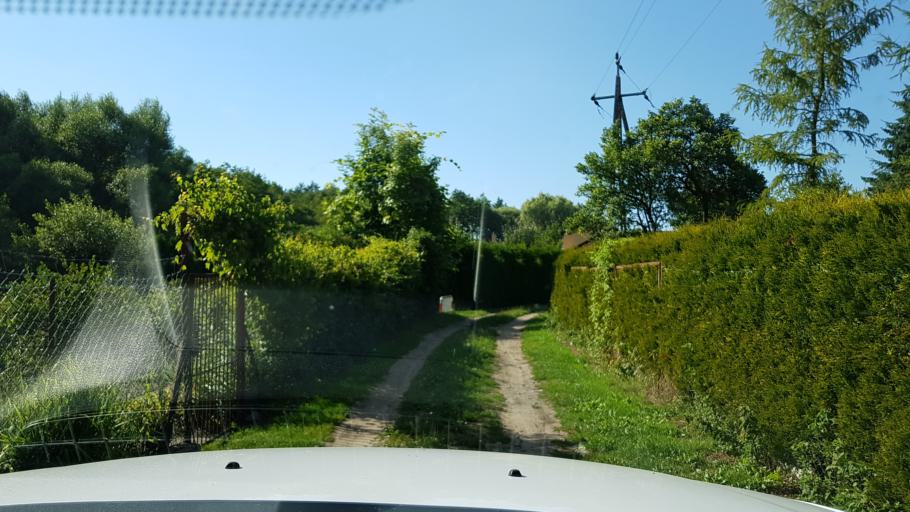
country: PL
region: West Pomeranian Voivodeship
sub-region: Powiat gryfinski
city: Banie
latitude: 53.0986
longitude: 14.6605
